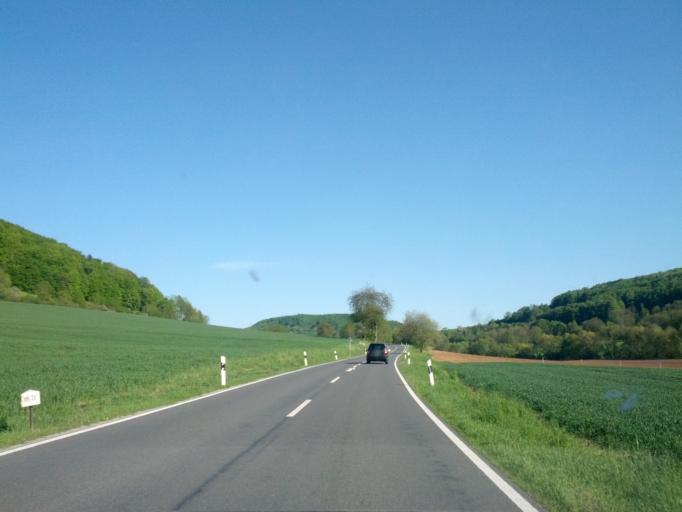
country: DE
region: Thuringia
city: Geismar
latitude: 51.2230
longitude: 10.1890
